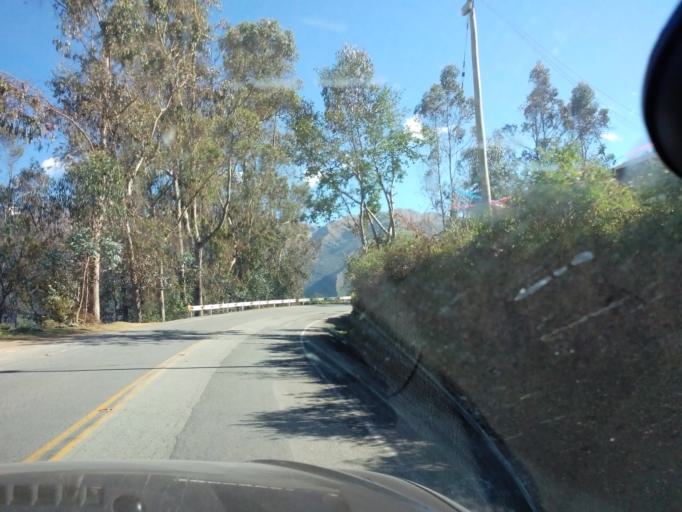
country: PE
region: Apurimac
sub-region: Provincia de Abancay
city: Tamburco
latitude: -13.5933
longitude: -72.8424
